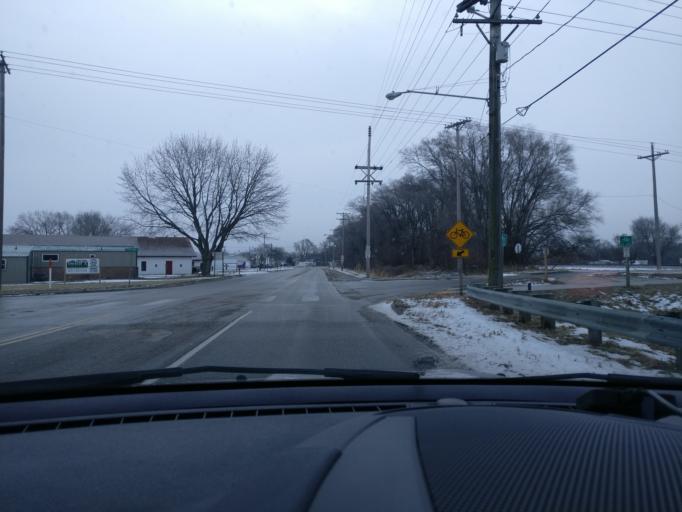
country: US
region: Nebraska
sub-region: Dodge County
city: Fremont
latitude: 41.4379
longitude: -96.5219
